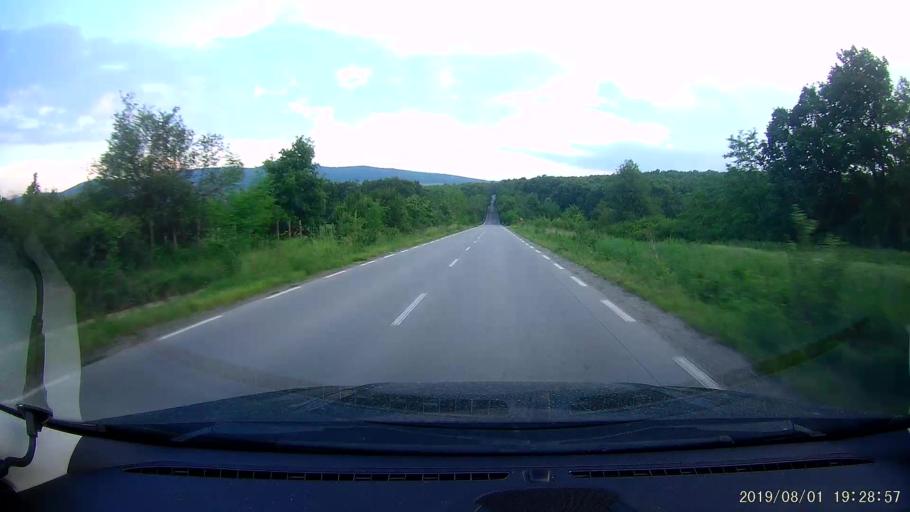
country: BG
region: Burgas
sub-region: Obshtina Sungurlare
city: Sungurlare
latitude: 42.8343
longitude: 26.9120
